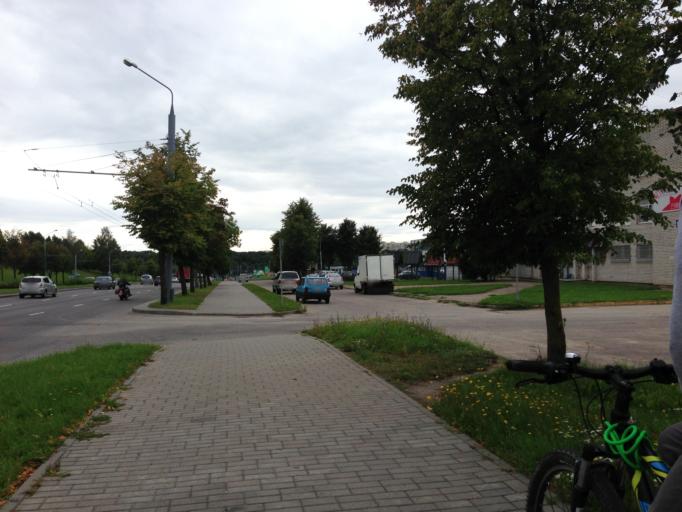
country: BY
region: Grodnenskaya
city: Hrodna
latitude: 53.6668
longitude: 23.8605
